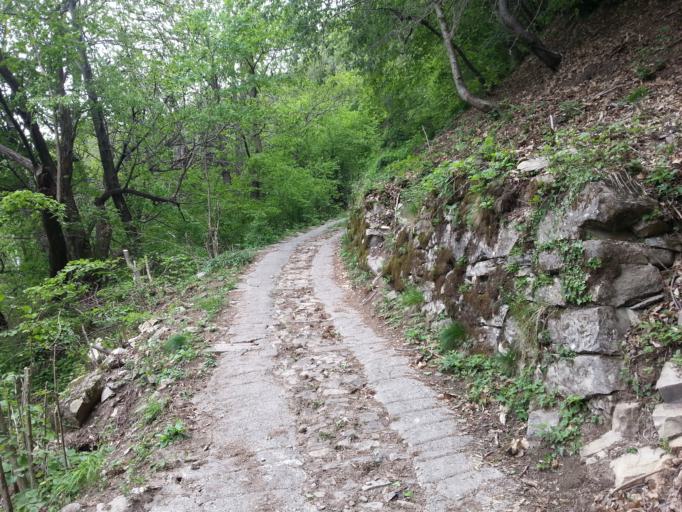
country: IT
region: Lombardy
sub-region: Provincia di Como
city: Ossuccio
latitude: 45.9885
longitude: 9.1776
